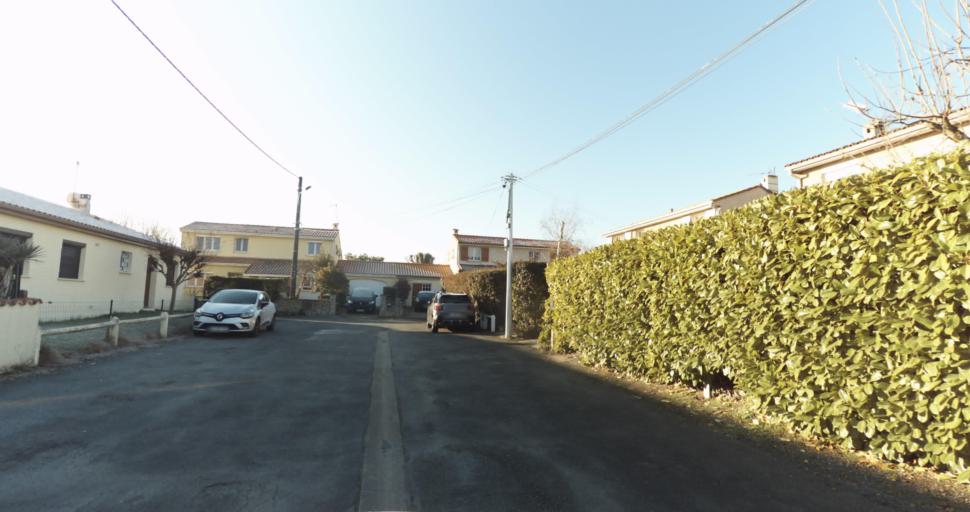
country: FR
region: Aquitaine
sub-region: Departement de la Gironde
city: Carbon-Blanc
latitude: 44.8994
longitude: -0.5067
